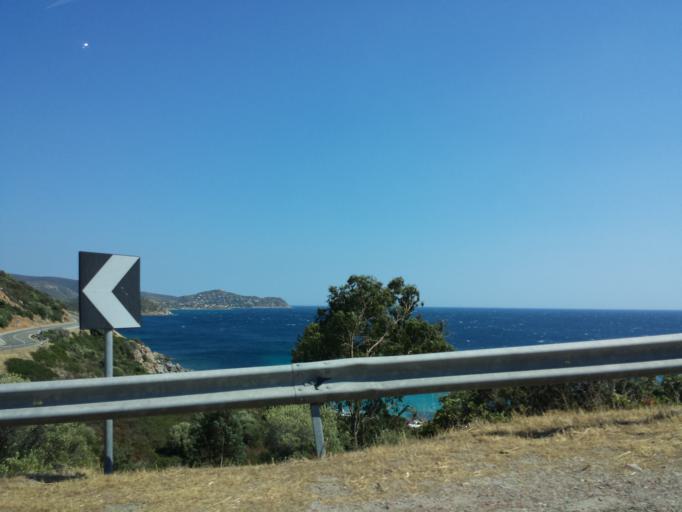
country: IT
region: Sardinia
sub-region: Provincia di Cagliari
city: Quartu Sant'Elena
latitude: 39.1805
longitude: 9.3540
